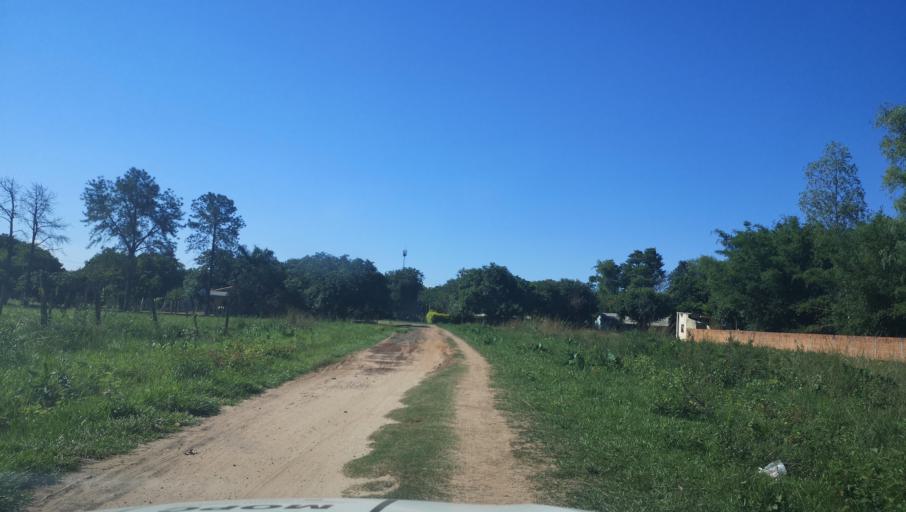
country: PY
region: Caaguazu
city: Carayao
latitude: -25.2001
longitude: -56.3959
